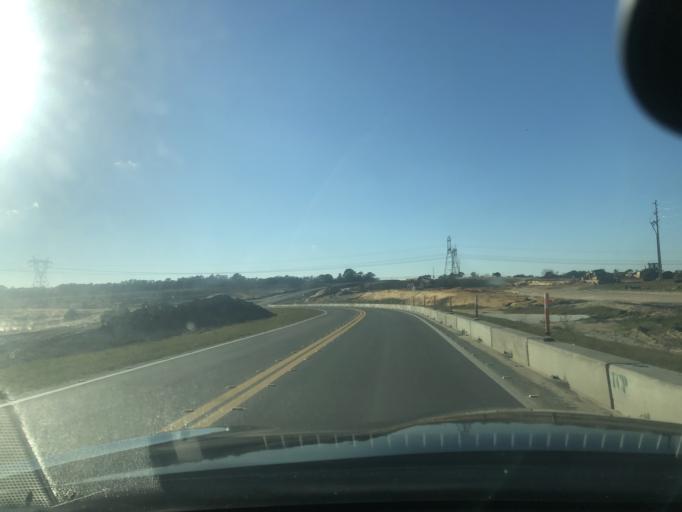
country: US
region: Florida
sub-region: Citrus County
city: Sugarmill Woods
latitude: 28.7639
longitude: -82.4961
